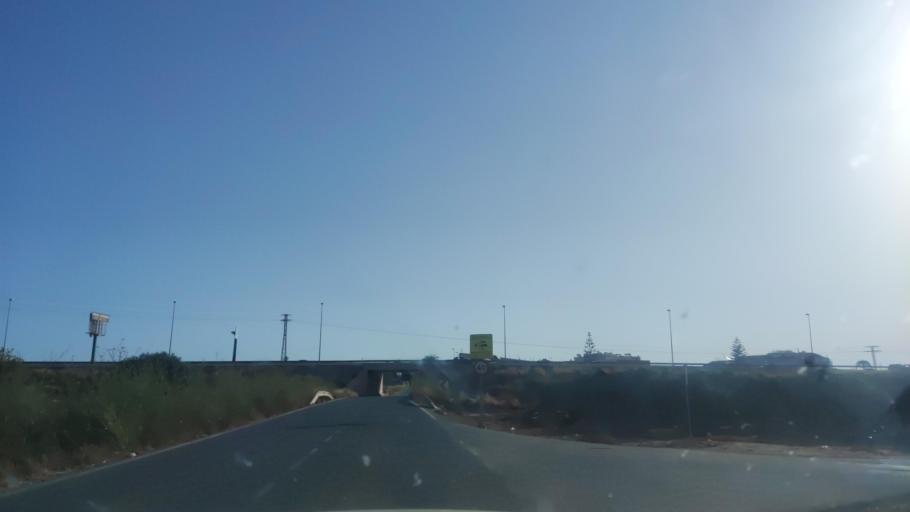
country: ES
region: Murcia
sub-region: Murcia
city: San Javier
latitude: 37.8050
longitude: -0.8597
